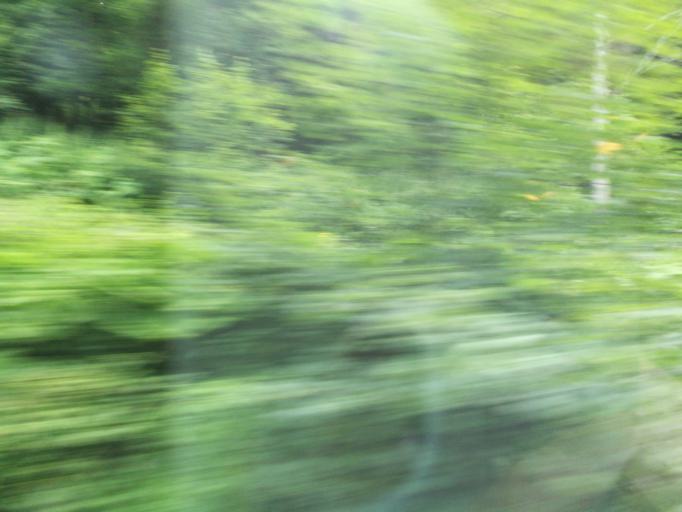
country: RO
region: Brasov
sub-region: Oras Predeal
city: Predeal
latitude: 45.5177
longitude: 25.5956
